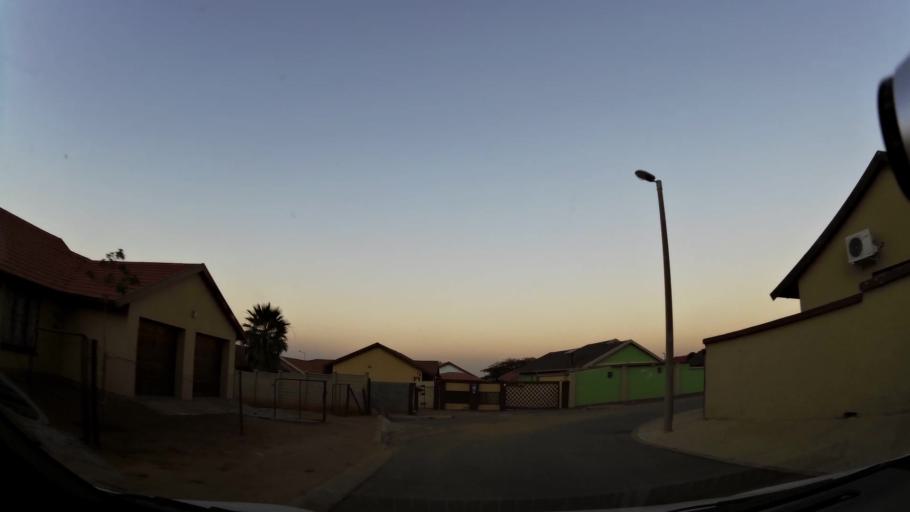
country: ZA
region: North-West
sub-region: Bojanala Platinum District Municipality
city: Rustenburg
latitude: -25.6516
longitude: 27.2032
